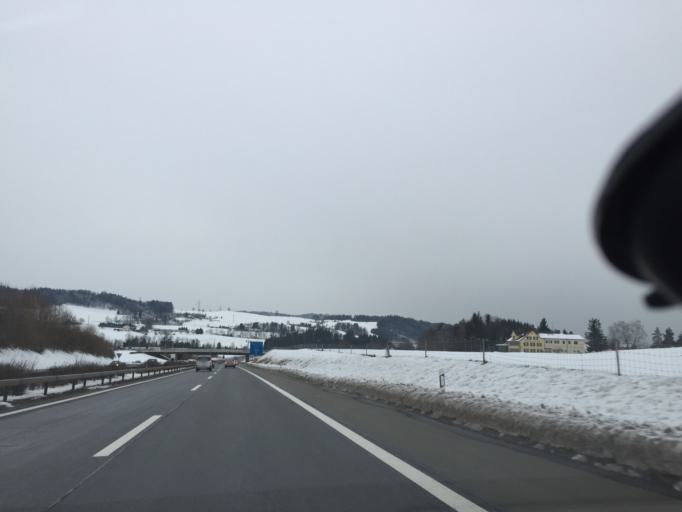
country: CH
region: Zurich
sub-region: Bezirk Horgen
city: Au
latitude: 47.2302
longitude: 8.6378
